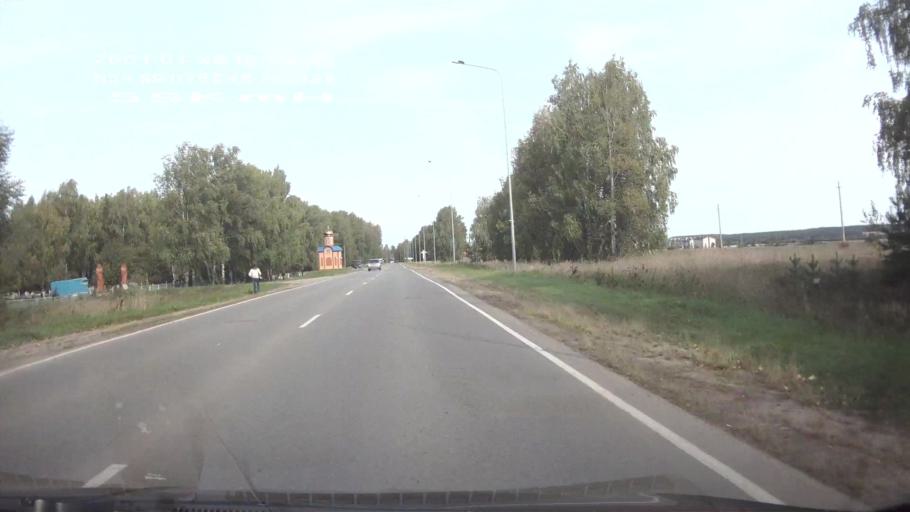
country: RU
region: Mariy-El
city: Kuzhener
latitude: 56.9916
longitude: 48.7433
